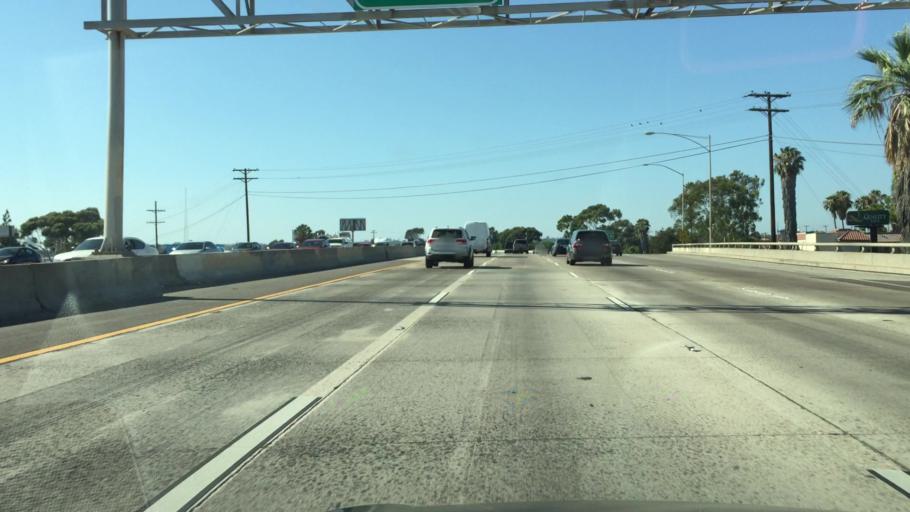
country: US
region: California
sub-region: San Diego County
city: National City
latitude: 32.6819
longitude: -117.1108
